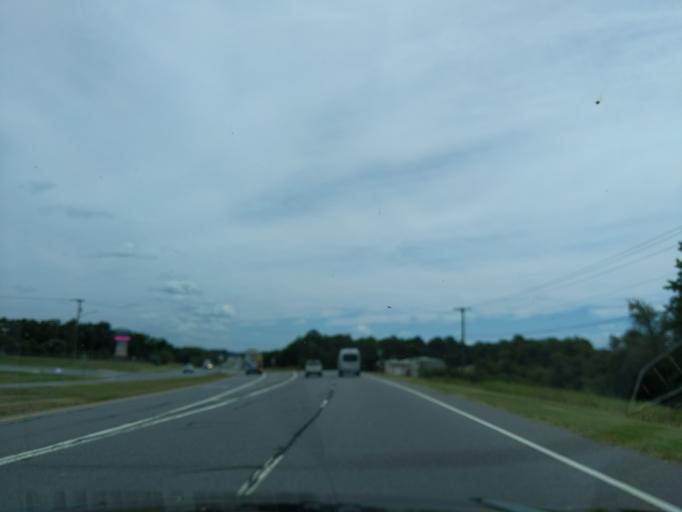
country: US
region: North Carolina
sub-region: Cabarrus County
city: Mount Pleasant
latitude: 35.3862
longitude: -80.5002
